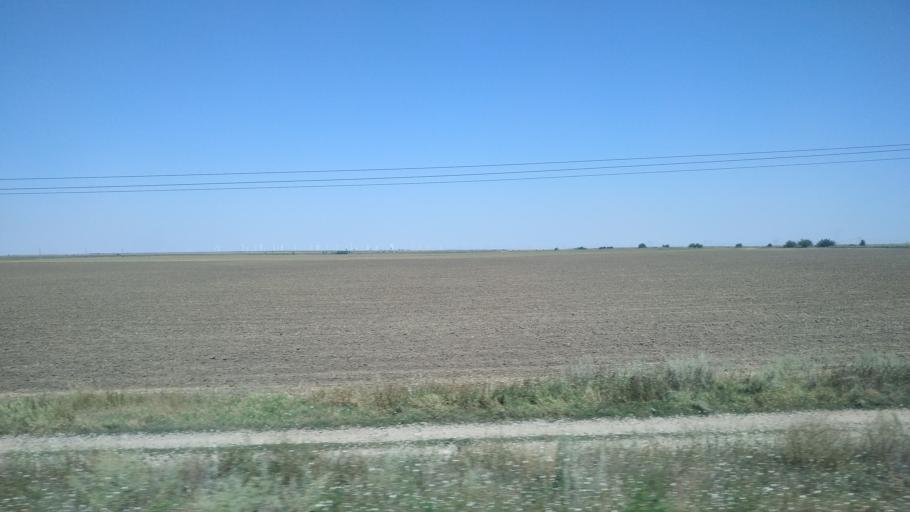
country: RO
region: Ialomita
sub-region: Municipiul Fetesti
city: Fetesti-Gara
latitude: 44.4182
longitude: 27.7795
